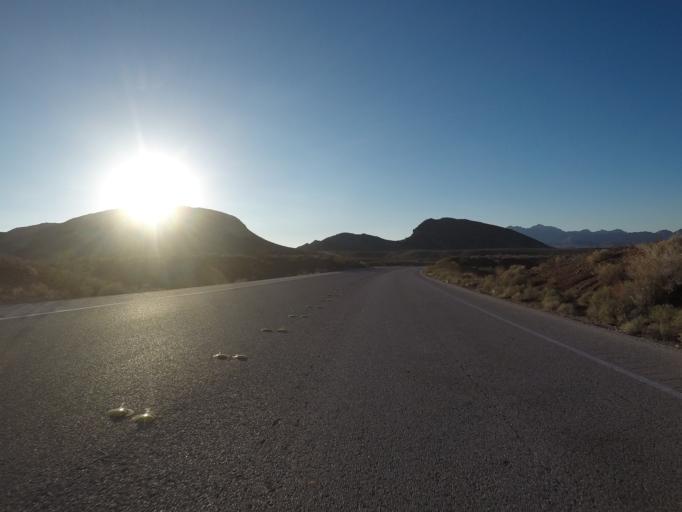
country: US
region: Nevada
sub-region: Clark County
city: Moapa Valley
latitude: 36.2427
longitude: -114.5411
